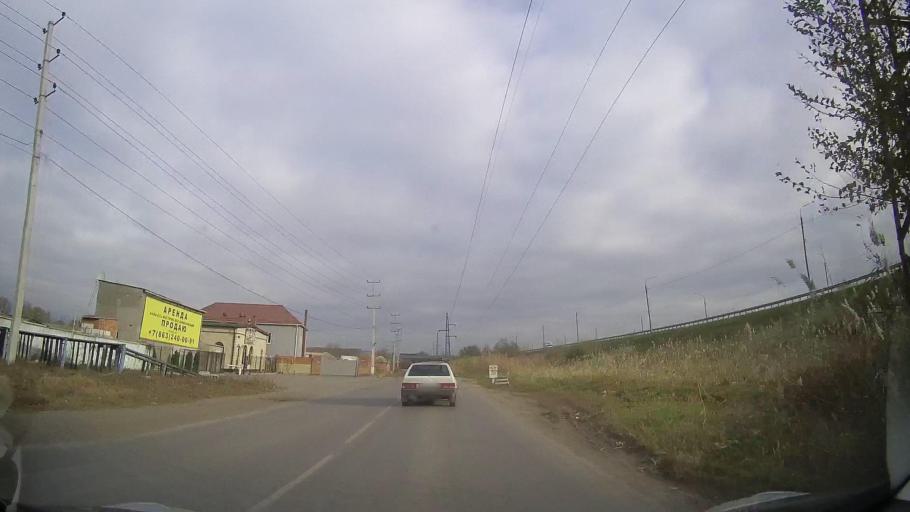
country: RU
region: Rostov
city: Bataysk
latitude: 47.1174
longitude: 39.7690
